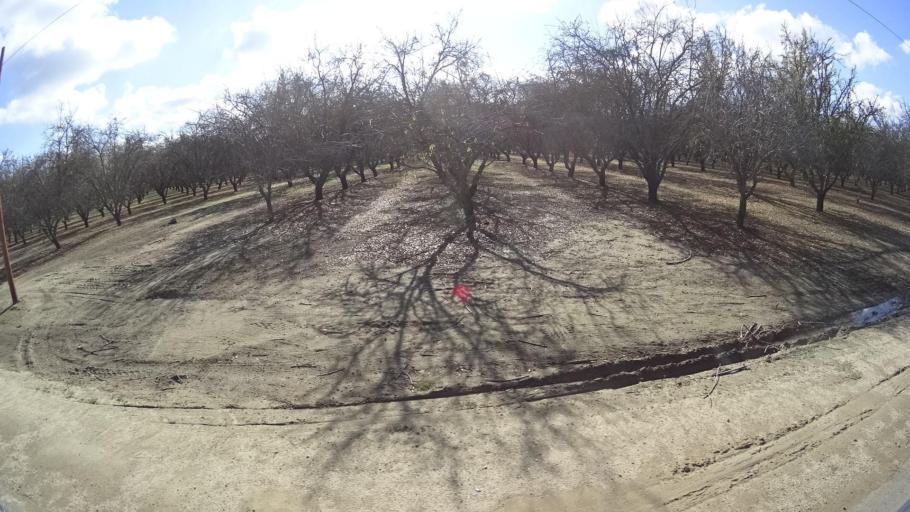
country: US
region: California
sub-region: Kern County
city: McFarland
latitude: 35.6887
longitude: -119.2964
